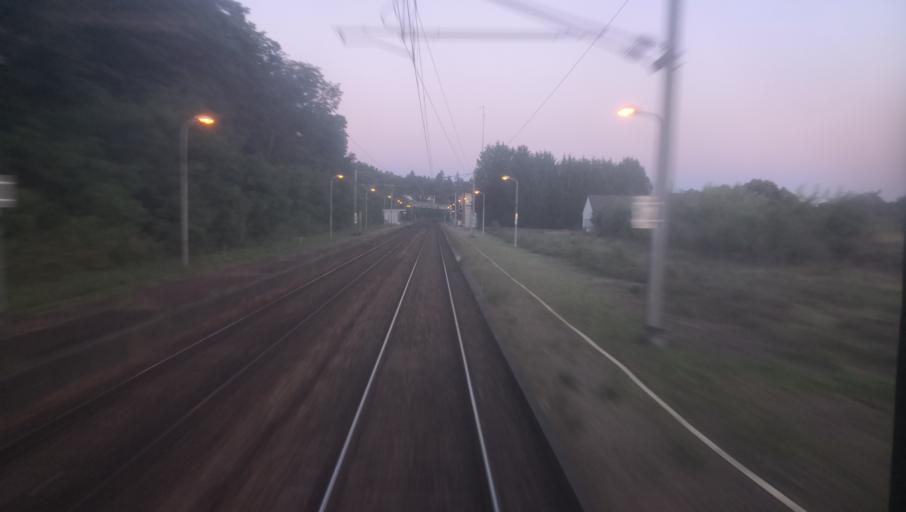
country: FR
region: Centre
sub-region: Departement du Loiret
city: Briare
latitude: 47.6476
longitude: 2.7320
